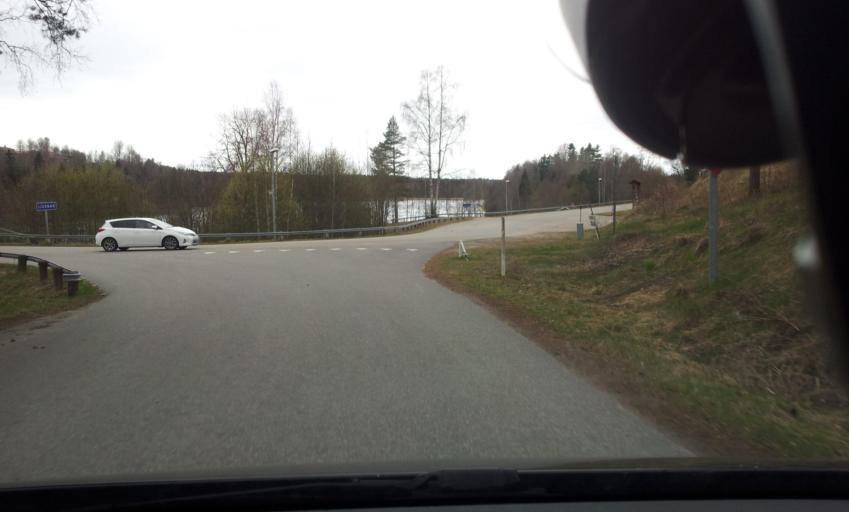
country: SE
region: Gaevleborg
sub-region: Ljusdals Kommun
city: Farila
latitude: 61.8061
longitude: 15.8508
